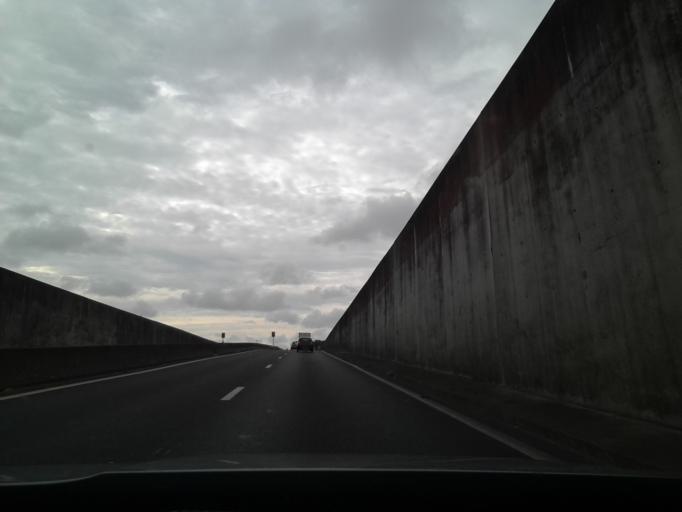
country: FR
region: Lower Normandy
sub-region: Departement de la Manche
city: Saint-Hilaire-Petitville
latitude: 49.3135
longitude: -1.2287
